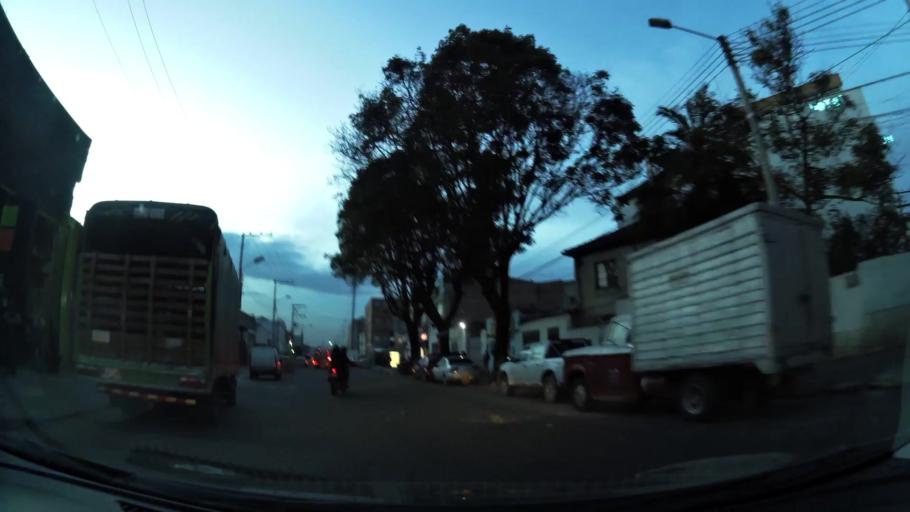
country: CO
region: Bogota D.C.
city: Bogota
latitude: 4.6521
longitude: -74.0659
